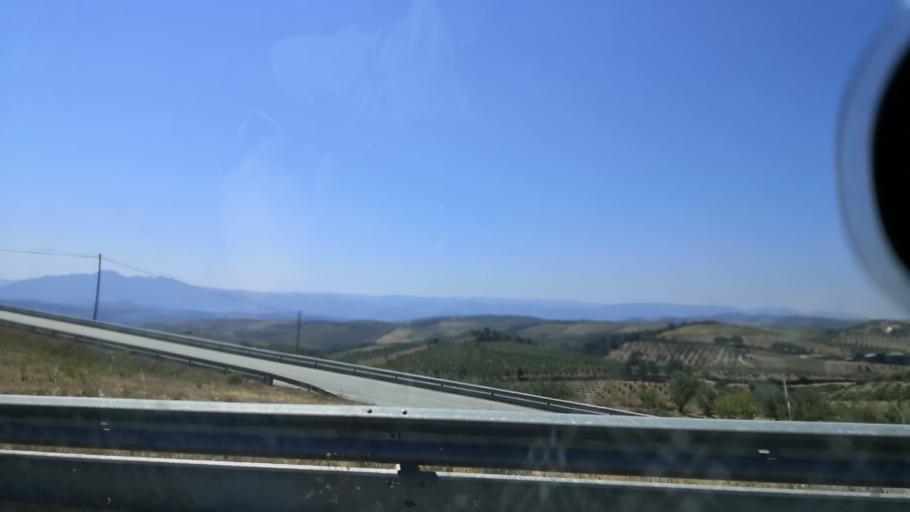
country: PT
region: Braganca
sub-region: Mirandela
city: Mirandela
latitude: 41.4515
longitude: -7.2821
